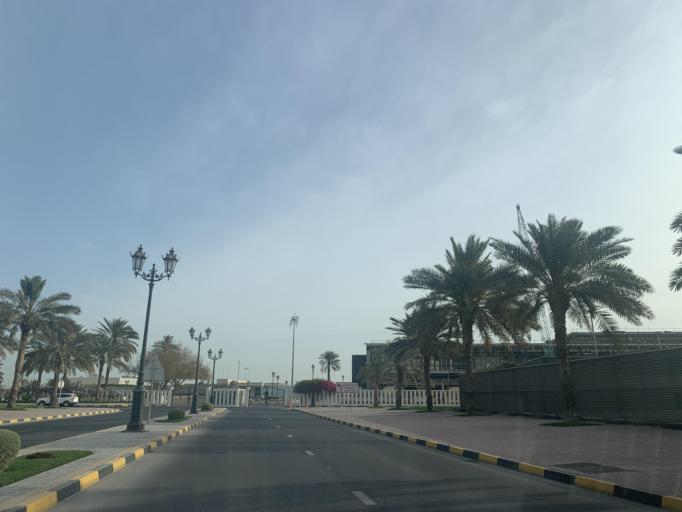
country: BH
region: Muharraq
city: Al Muharraq
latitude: 26.2701
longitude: 50.6235
